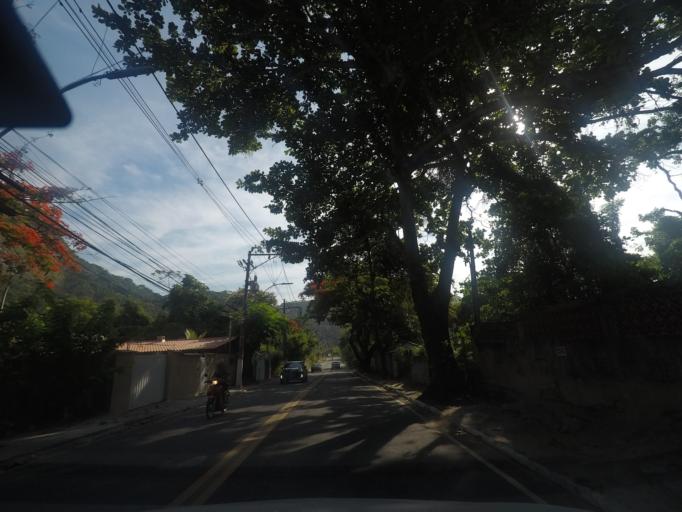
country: BR
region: Rio de Janeiro
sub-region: Niteroi
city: Niteroi
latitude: -22.9643
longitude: -43.0164
